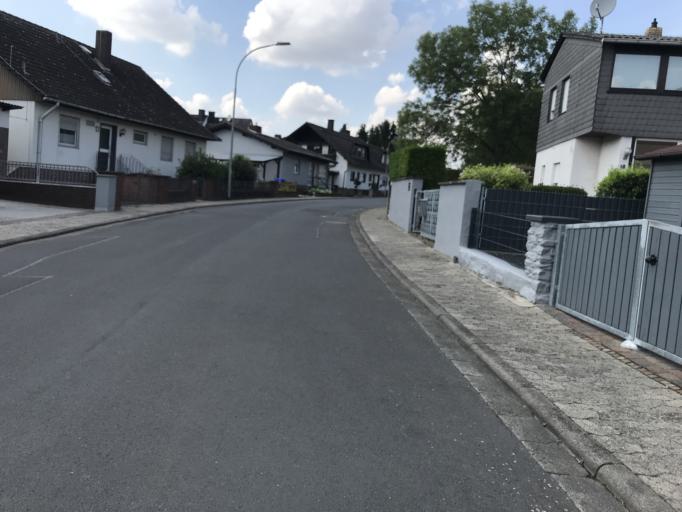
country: DE
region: Hesse
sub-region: Regierungsbezirk Darmstadt
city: Wolfersheim
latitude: 50.3940
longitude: 8.8080
